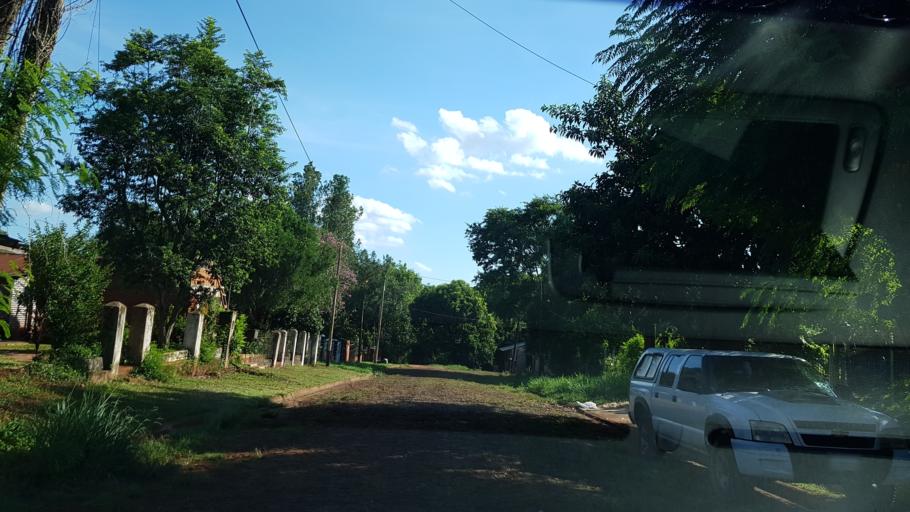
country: AR
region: Misiones
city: Puerto Libertad
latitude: -25.9198
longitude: -54.5780
